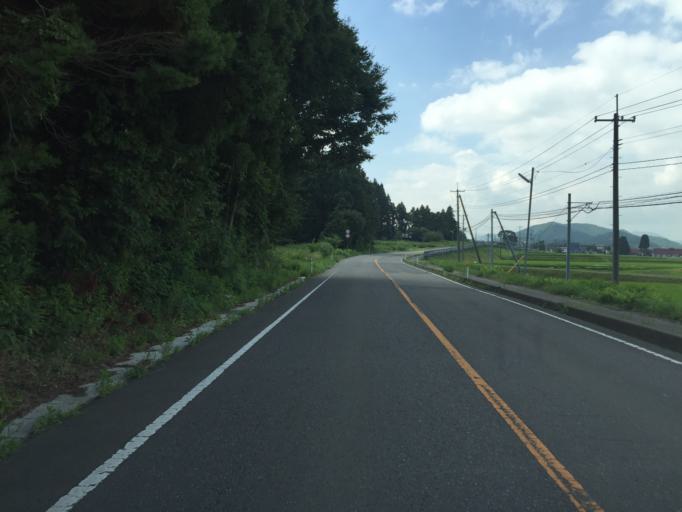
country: JP
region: Fukushima
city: Inawashiro
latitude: 37.4280
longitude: 140.1476
